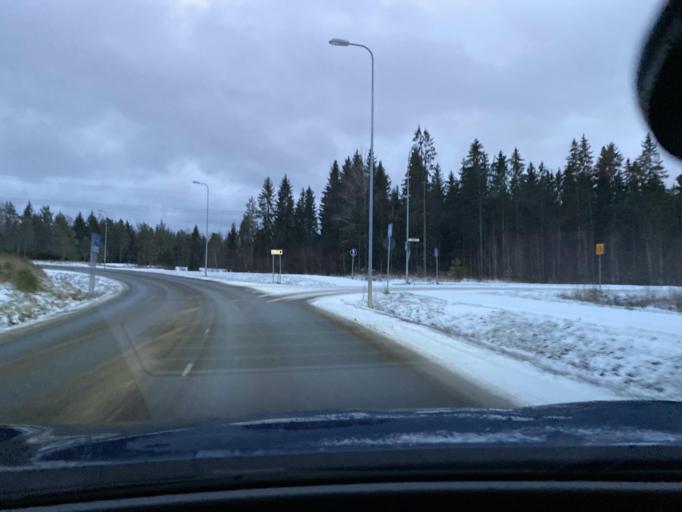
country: FI
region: Satakunta
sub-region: Rauma
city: Rauma
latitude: 61.1463
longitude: 21.5704
